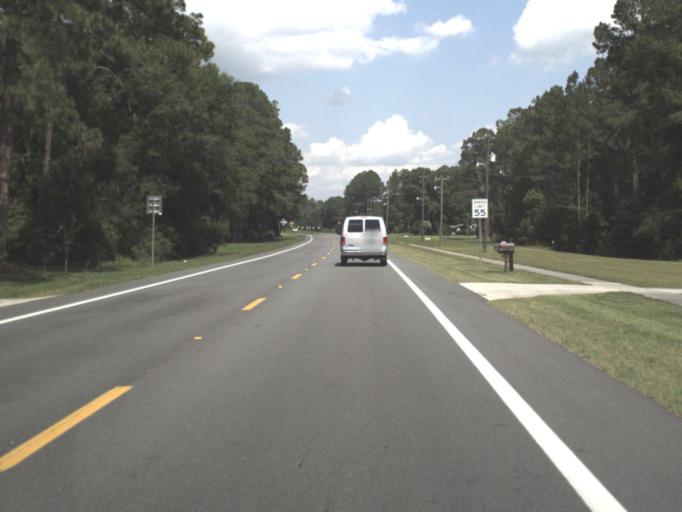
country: US
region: Florida
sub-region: Bradford County
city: Starke
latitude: 29.9395
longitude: -82.0926
